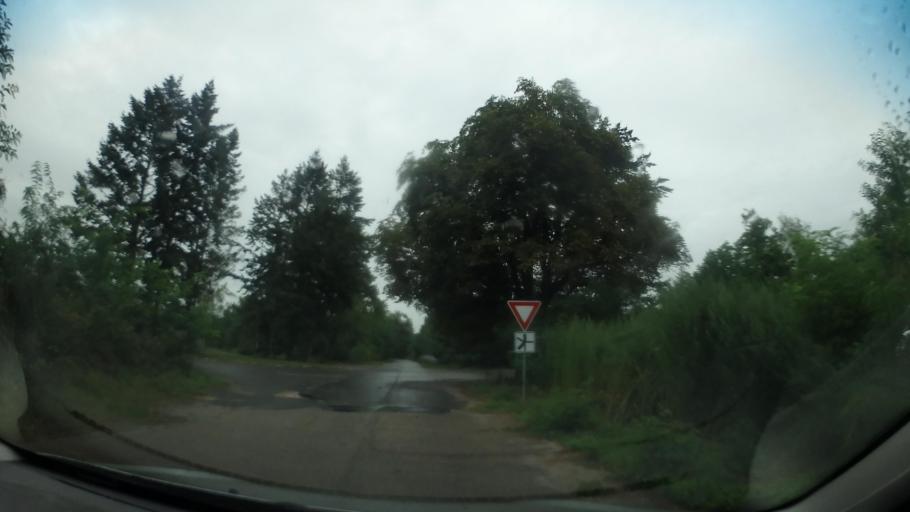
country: CZ
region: Central Bohemia
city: Milovice
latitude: 50.2417
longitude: 14.9173
